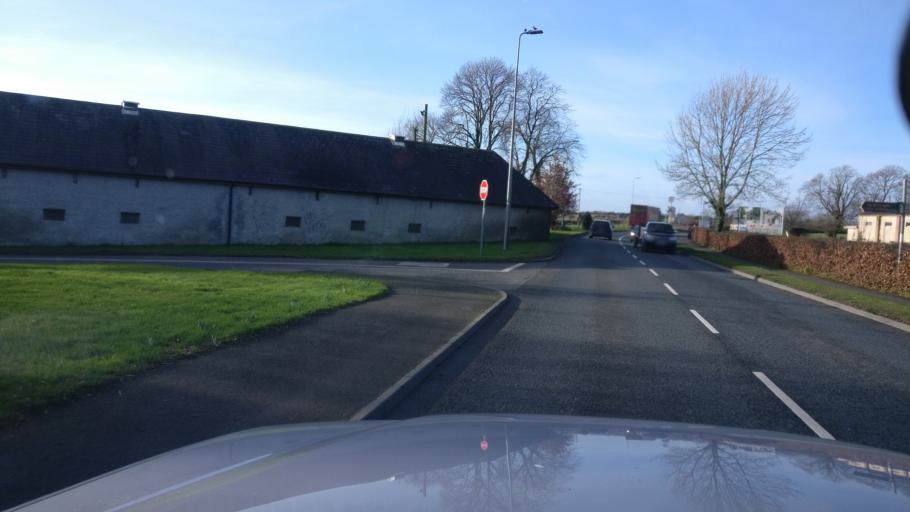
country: IE
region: Leinster
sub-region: Uibh Fhaili
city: Tullamore
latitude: 53.2146
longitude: -7.4531
